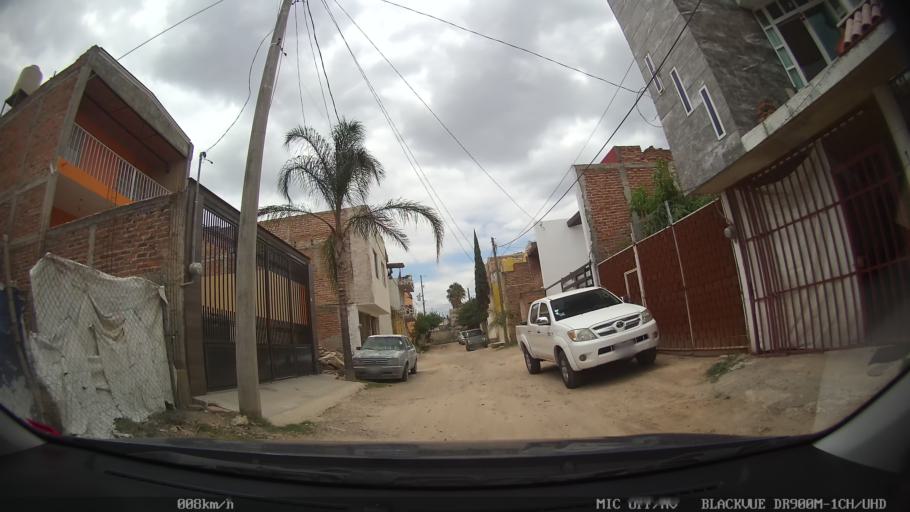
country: MX
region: Jalisco
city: Tonala
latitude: 20.6401
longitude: -103.2499
